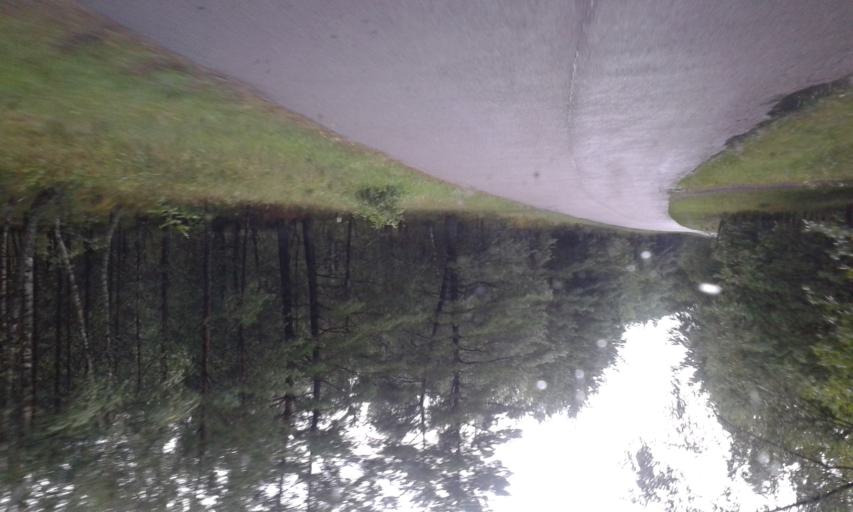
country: PL
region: West Pomeranian Voivodeship
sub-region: Powiat szczecinecki
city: Borne Sulinowo
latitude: 53.5424
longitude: 16.5108
